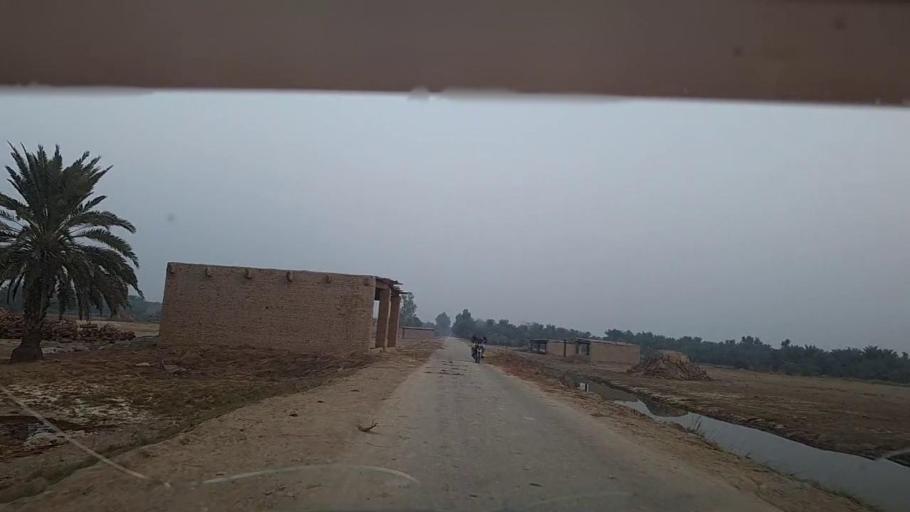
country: PK
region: Sindh
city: Khairpur
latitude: 27.5769
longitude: 68.7198
